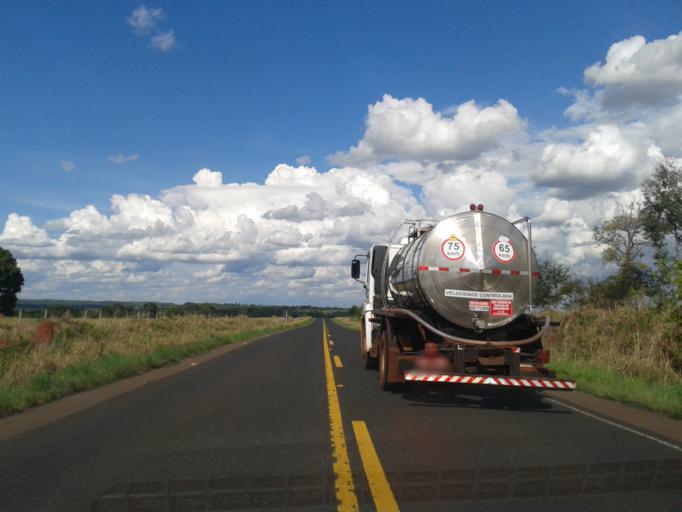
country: BR
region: Minas Gerais
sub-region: Campina Verde
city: Campina Verde
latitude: -19.5583
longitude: -49.8233
